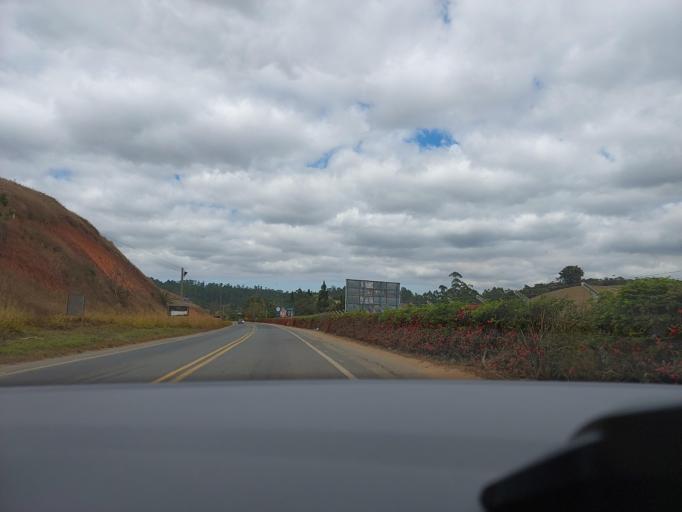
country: BR
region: Minas Gerais
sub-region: Vicosa
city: Vicosa
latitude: -20.7897
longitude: -42.8388
